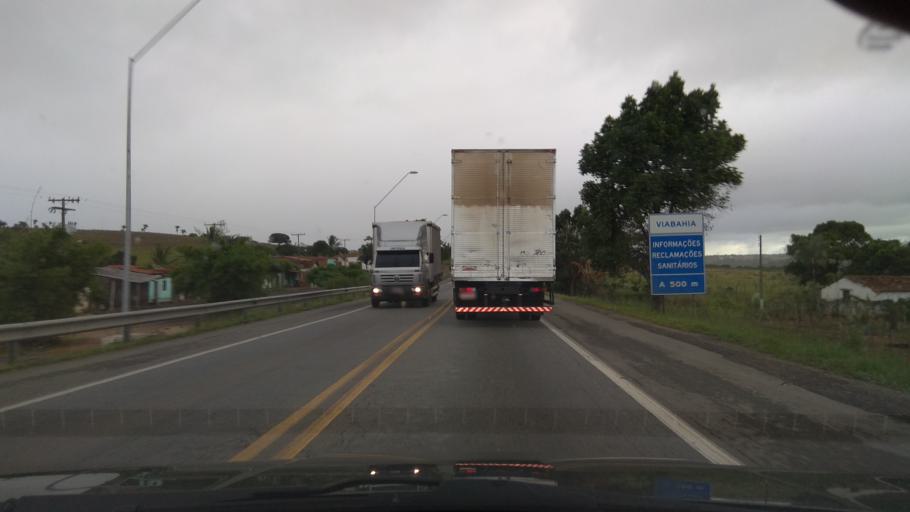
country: BR
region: Bahia
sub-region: Jaguaquara
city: Jaguaquara
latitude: -13.4806
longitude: -40.0422
